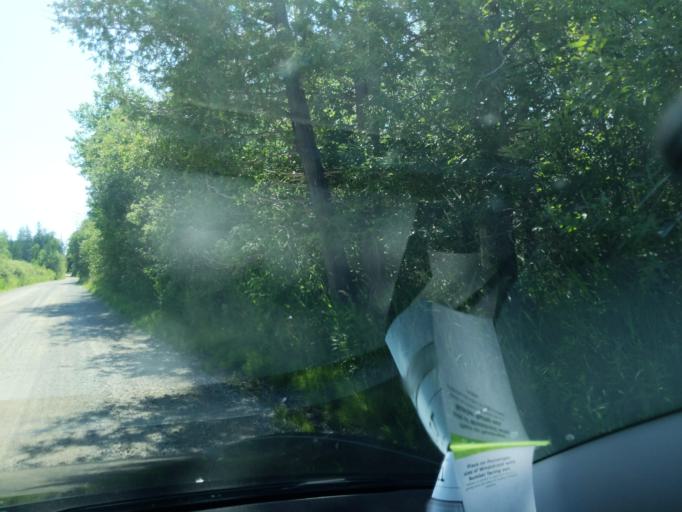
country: US
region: Michigan
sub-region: Mackinac County
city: Saint Ignace
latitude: 45.6795
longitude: -84.6972
